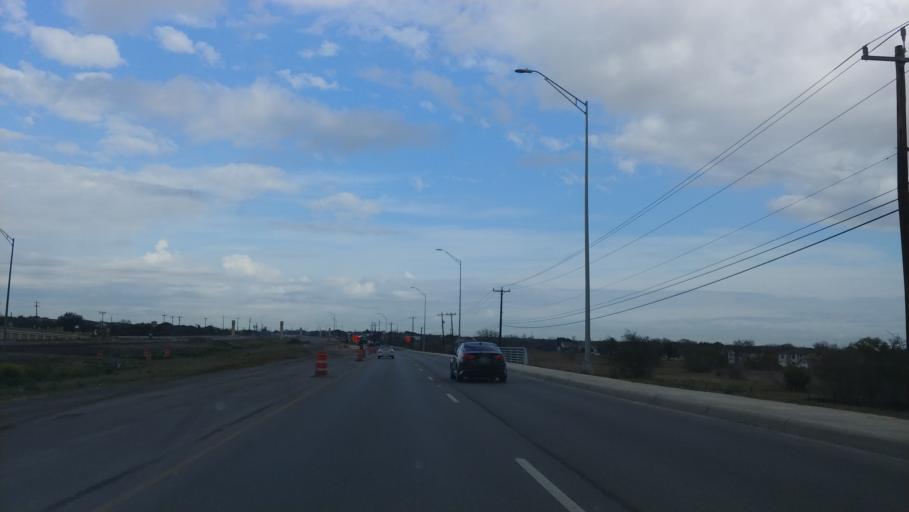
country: US
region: Texas
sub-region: Bexar County
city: Lackland Air Force Base
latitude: 29.3884
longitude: -98.7012
